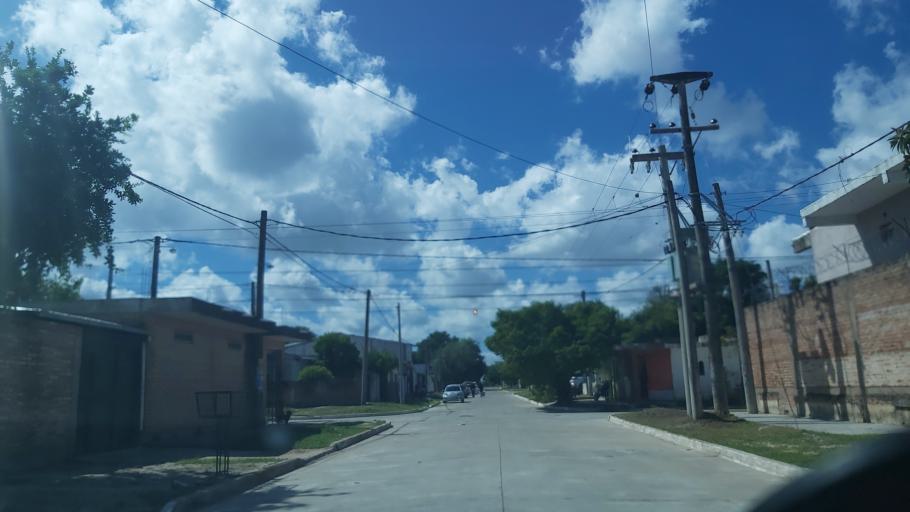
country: AR
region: Corrientes
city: Corrientes
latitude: -27.4789
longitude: -58.8505
